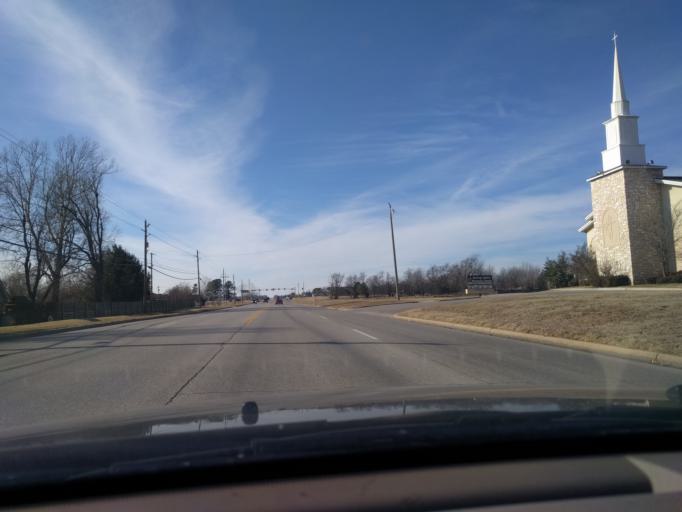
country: US
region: Oklahoma
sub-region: Tulsa County
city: Broken Arrow
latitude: 36.0609
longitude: -95.7225
